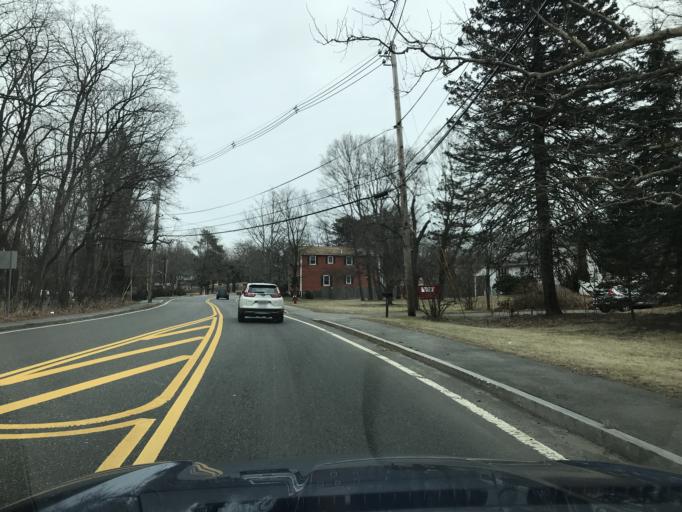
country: US
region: Massachusetts
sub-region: Essex County
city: Lynnfield
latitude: 42.5126
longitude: -71.0271
